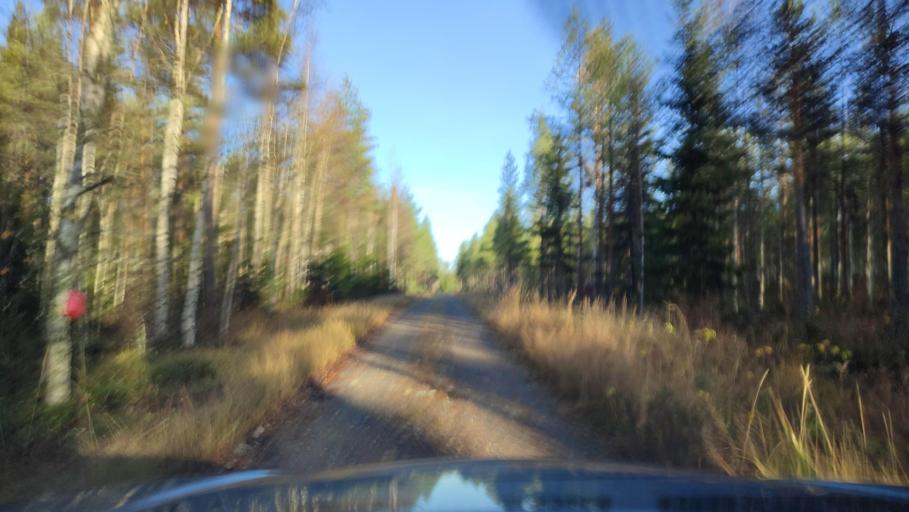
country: FI
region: Southern Ostrobothnia
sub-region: Suupohja
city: Karijoki
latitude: 62.1909
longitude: 21.6069
